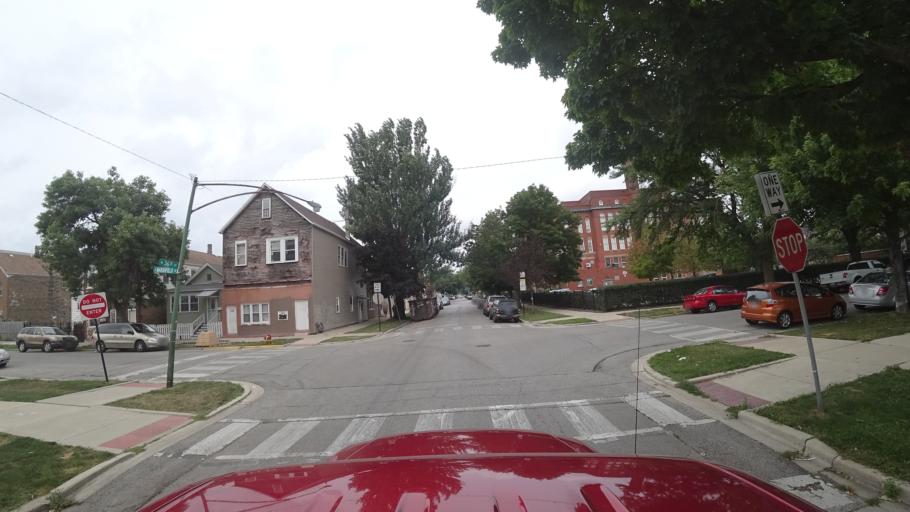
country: US
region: Illinois
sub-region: Cook County
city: Chicago
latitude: 41.8287
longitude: -87.6665
